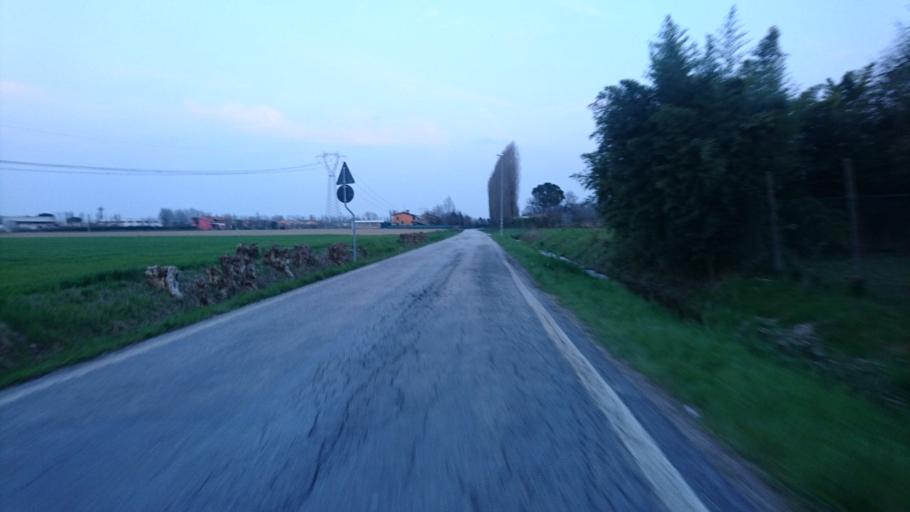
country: IT
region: Veneto
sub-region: Provincia di Padova
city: Saccolongo
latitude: 45.3907
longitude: 11.7537
